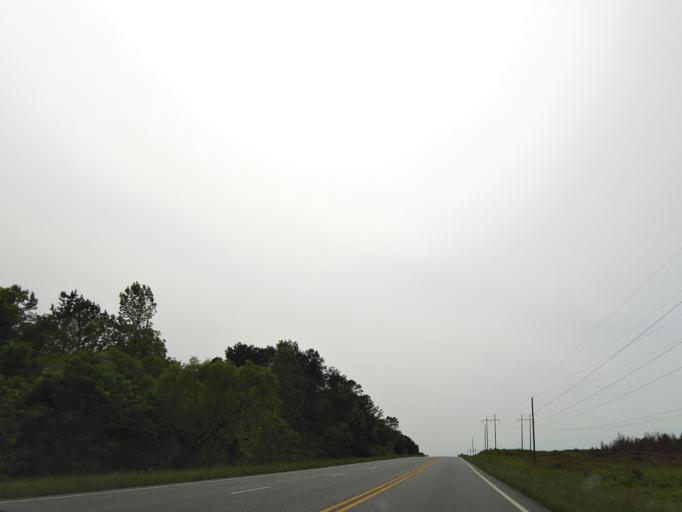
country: US
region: Georgia
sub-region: Houston County
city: Robins Air Force Base
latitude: 32.5408
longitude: -83.4735
